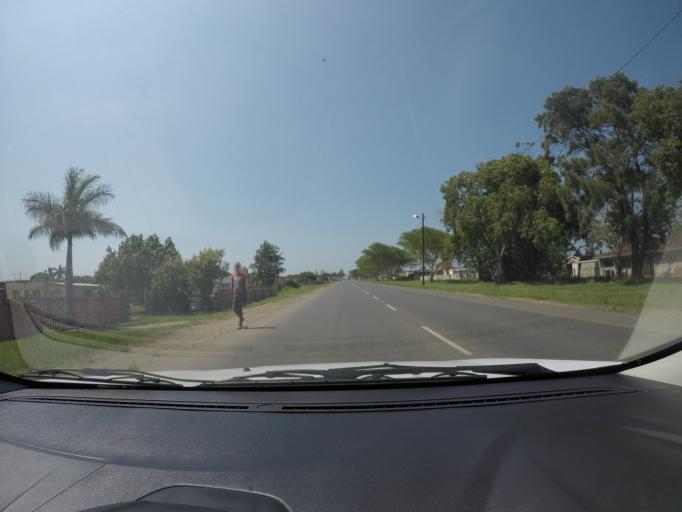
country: ZA
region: KwaZulu-Natal
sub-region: uThungulu District Municipality
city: eSikhawini
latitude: -28.8600
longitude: 31.9242
